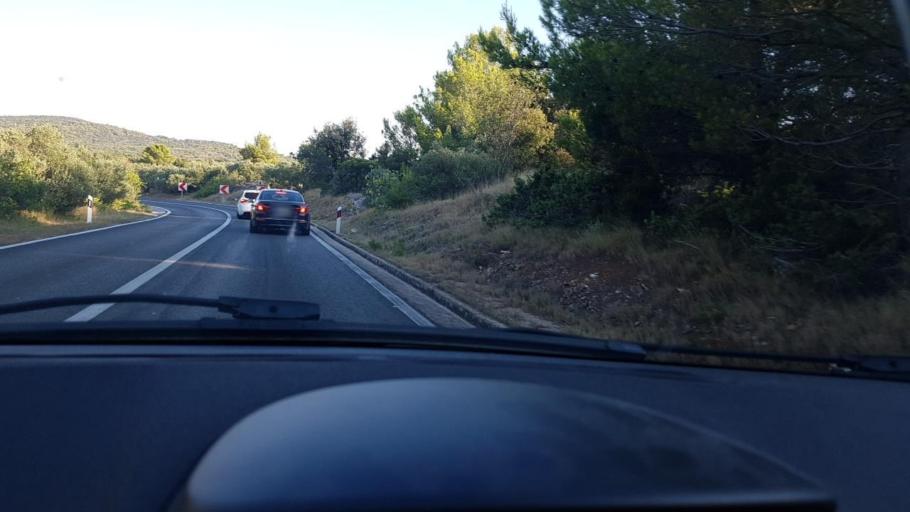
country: HR
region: Sibensko-Kniniska
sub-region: Grad Sibenik
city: Tisno
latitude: 43.7922
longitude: 15.6254
